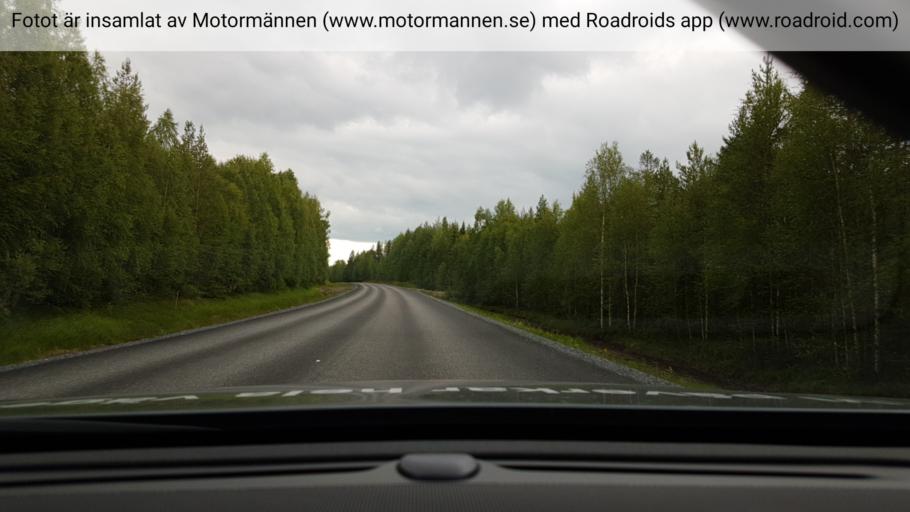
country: SE
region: Vaesterbotten
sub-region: Skelleftea Kommun
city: Boliden
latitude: 64.9074
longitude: 20.3474
